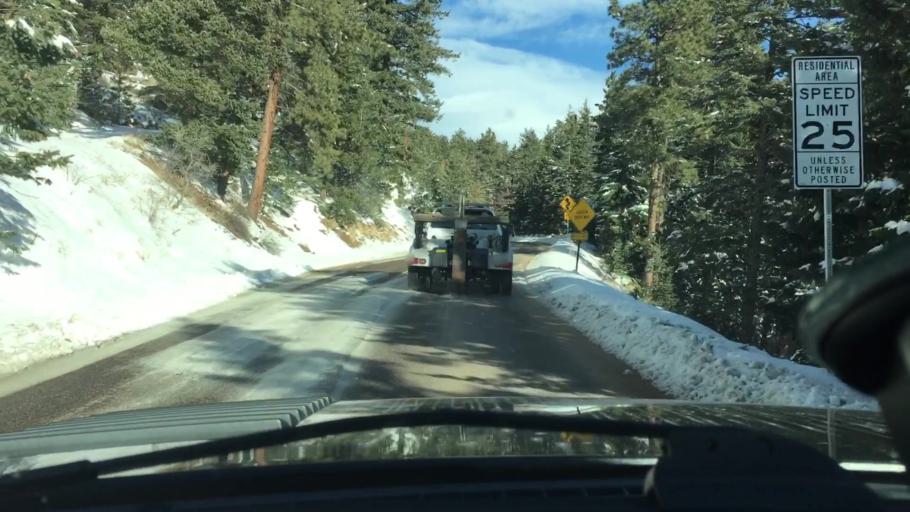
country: US
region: Colorado
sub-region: Jefferson County
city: Indian Hills
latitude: 39.5547
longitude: -105.2452
